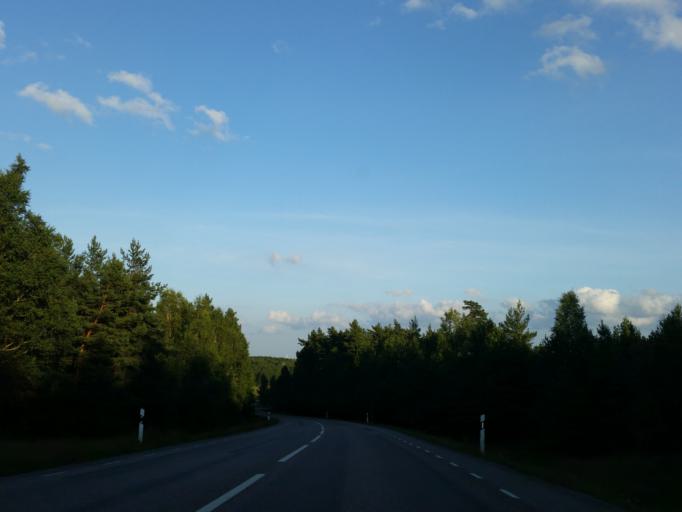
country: SE
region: Stockholm
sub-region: Sodertalje Kommun
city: Soedertaelje
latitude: 59.2302
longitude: 17.5530
